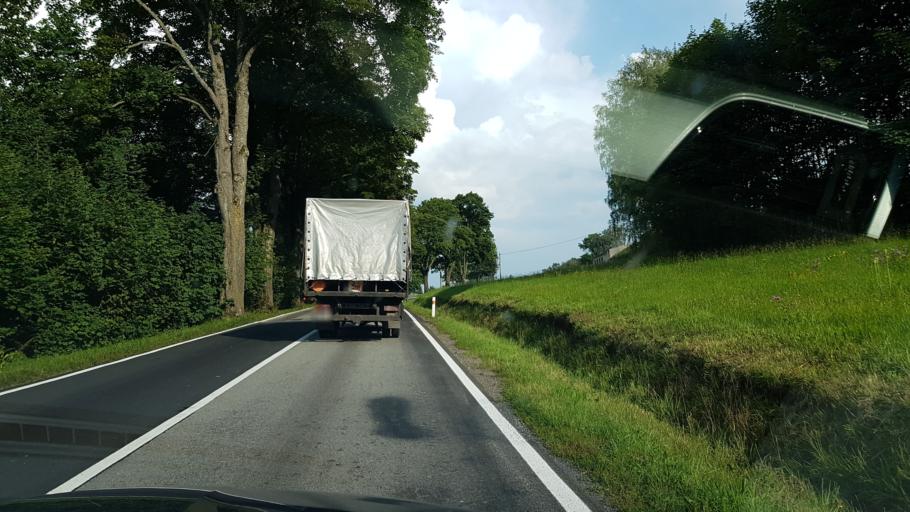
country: PL
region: Lower Silesian Voivodeship
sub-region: Powiat klodzki
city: Miedzylesie
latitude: 50.0993
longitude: 16.6341
